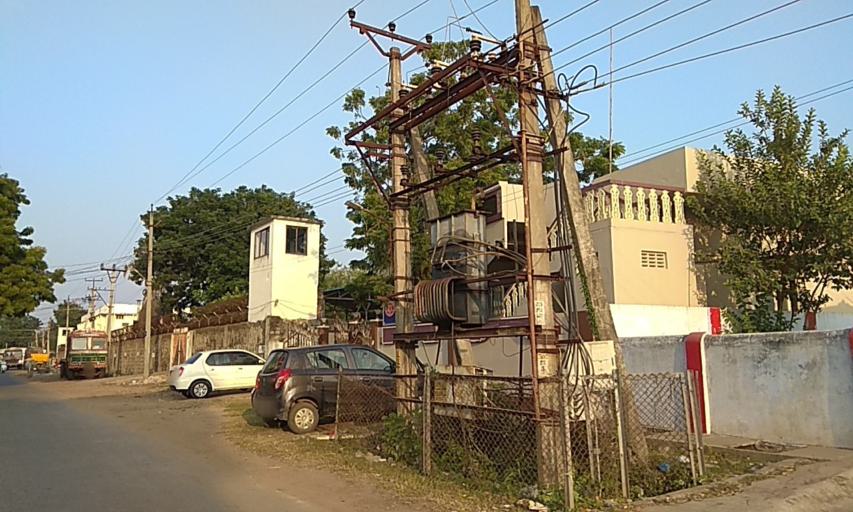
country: IN
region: Andhra Pradesh
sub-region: Krishna
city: Machilipatnam
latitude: 16.1878
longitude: 81.1346
